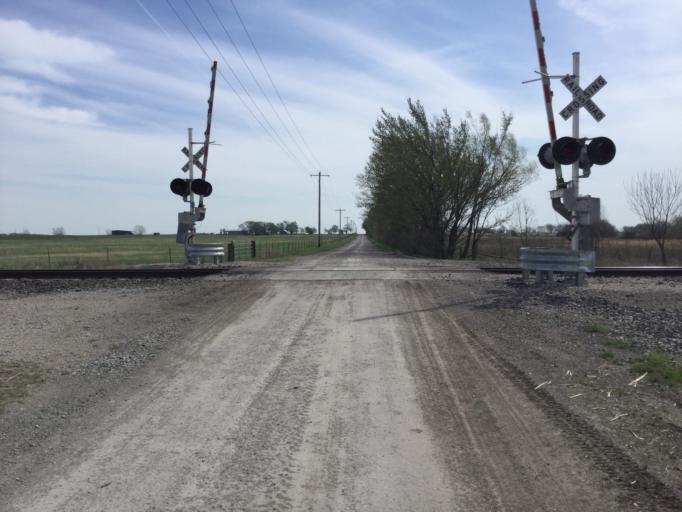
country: US
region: Kansas
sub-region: Labette County
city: Parsons
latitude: 37.4132
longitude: -95.2611
